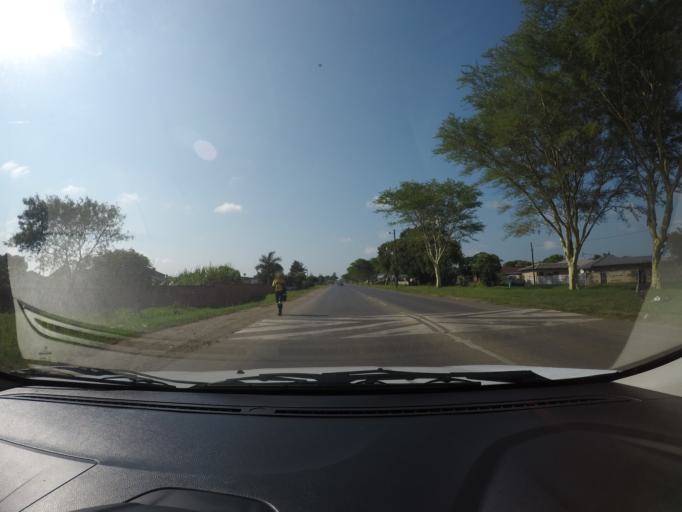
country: ZA
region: KwaZulu-Natal
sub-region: uThungulu District Municipality
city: eSikhawini
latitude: -28.8595
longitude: 31.9241
